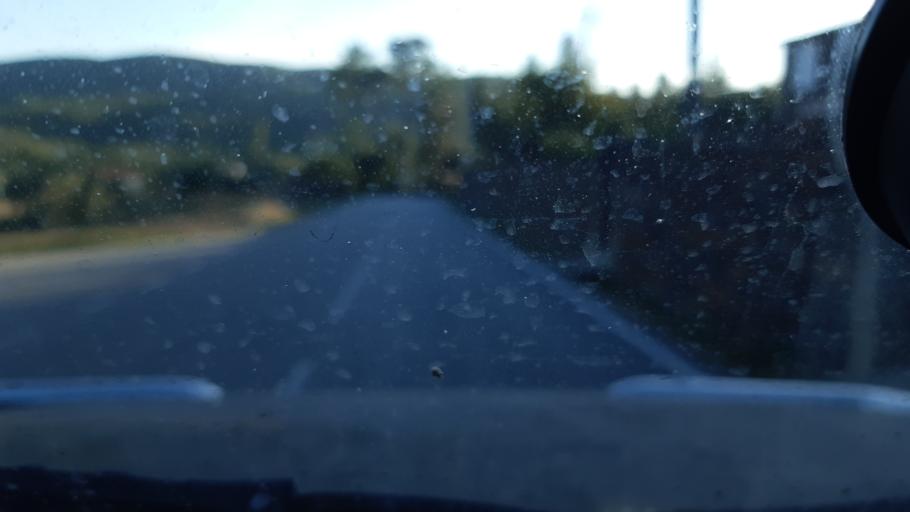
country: PT
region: Viseu
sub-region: Mortagua
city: Mortagua
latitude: 40.5469
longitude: -8.2619
